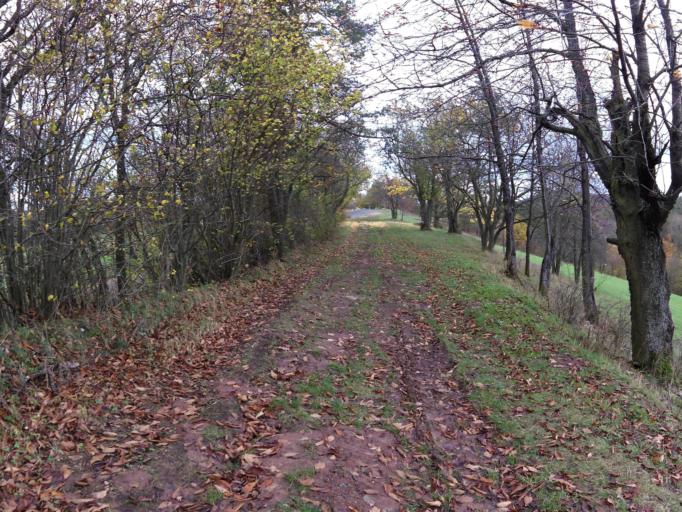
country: DE
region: Thuringia
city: Ifta
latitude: 51.0678
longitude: 10.1388
